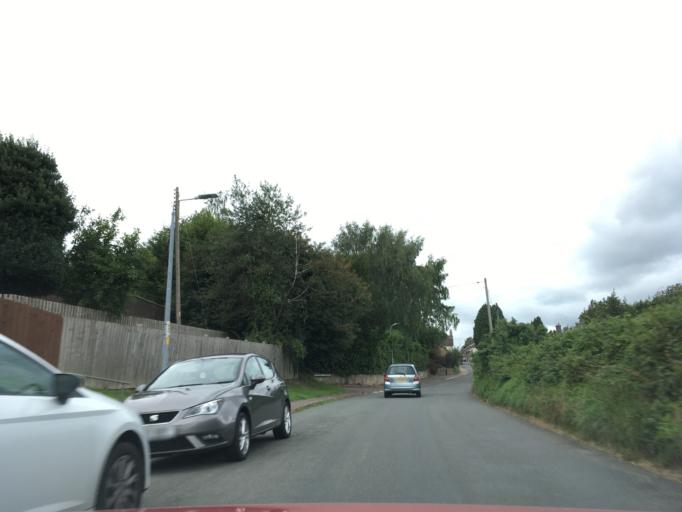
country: GB
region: Wales
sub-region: Monmouthshire
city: Caldicot
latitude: 51.6102
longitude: -2.7627
